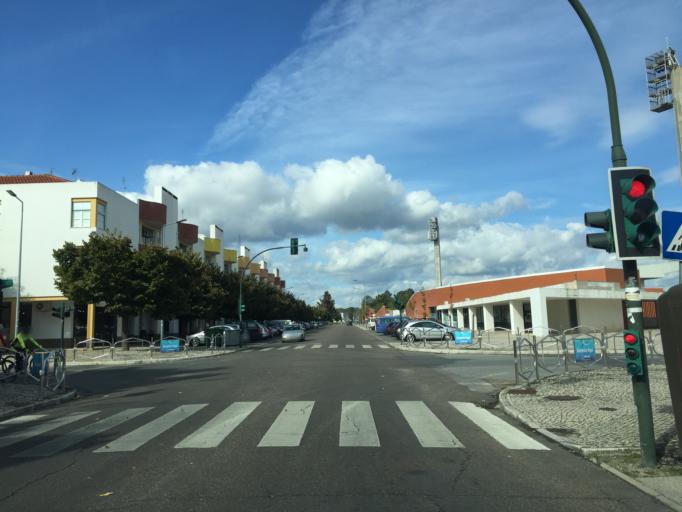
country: PT
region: Portalegre
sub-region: Ponte de Sor
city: Ponte de Sor
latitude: 39.2524
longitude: -8.0137
